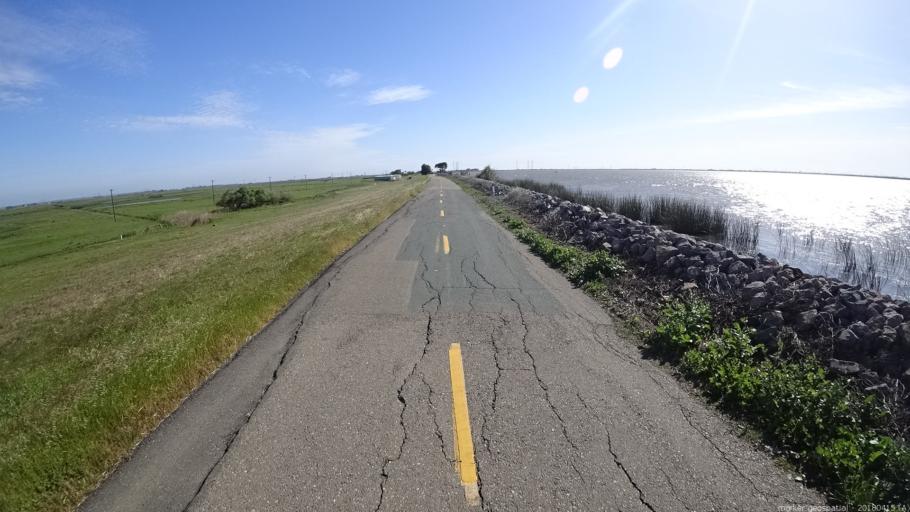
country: US
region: California
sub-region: Contra Costa County
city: Oakley
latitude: 38.0365
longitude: -121.7306
